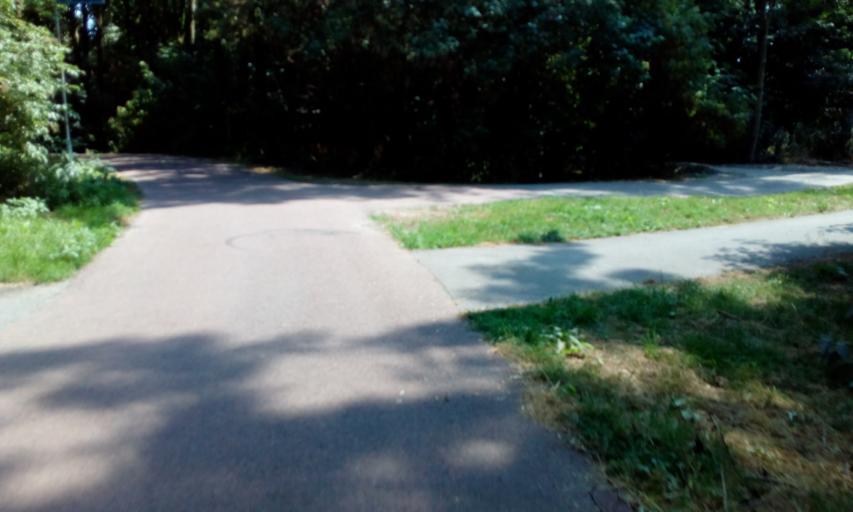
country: NL
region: South Holland
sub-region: Gemeente Capelle aan den IJssel
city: Capelle aan den IJssel
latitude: 51.9460
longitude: 4.5900
